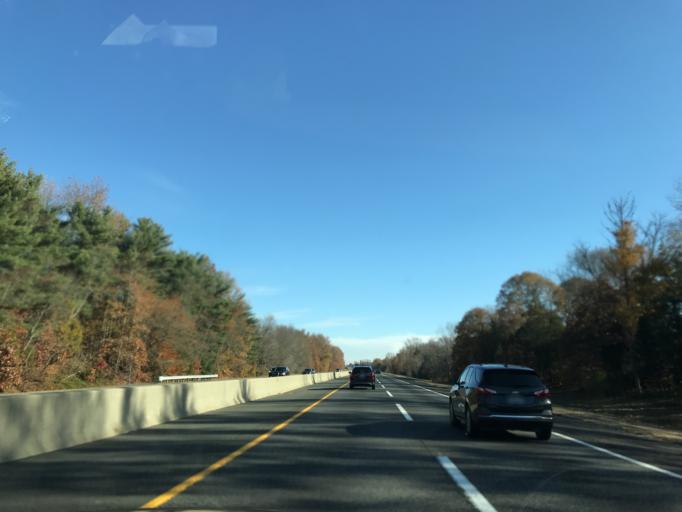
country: US
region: New Jersey
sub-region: Gloucester County
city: Swedesboro
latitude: 39.7213
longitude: -75.3316
